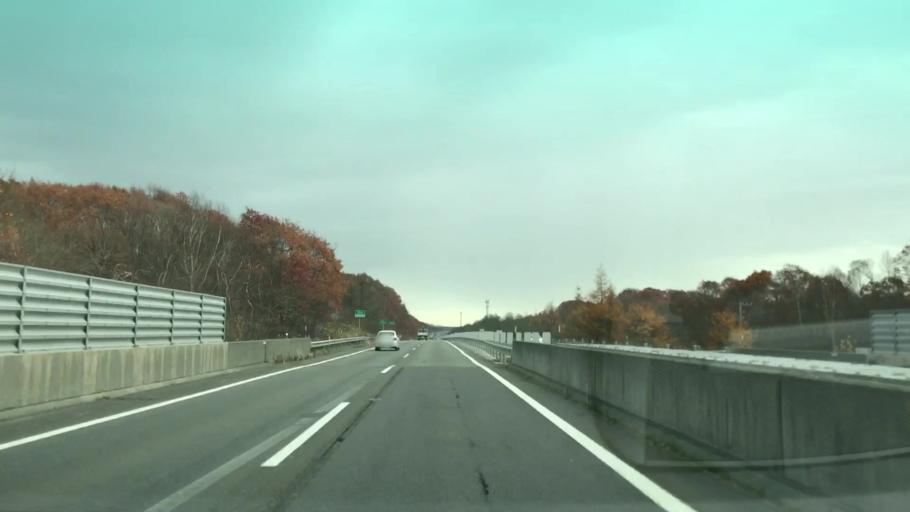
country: JP
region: Hokkaido
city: Tomakomai
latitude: 42.6629
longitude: 141.8110
